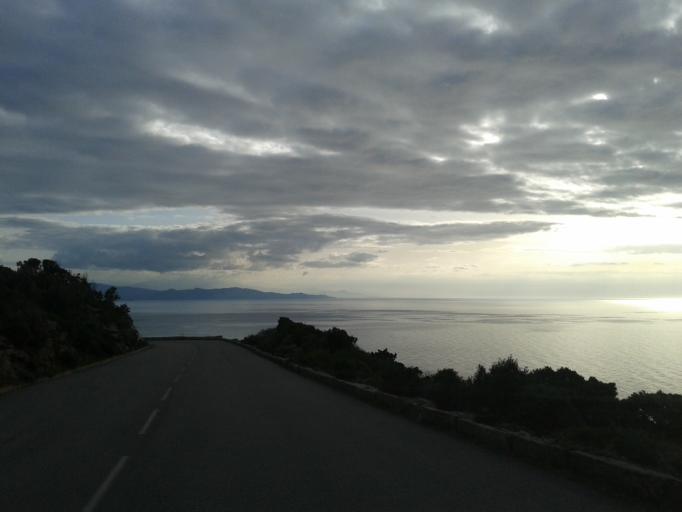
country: FR
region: Corsica
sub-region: Departement de la Haute-Corse
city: Brando
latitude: 42.8746
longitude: 9.3325
